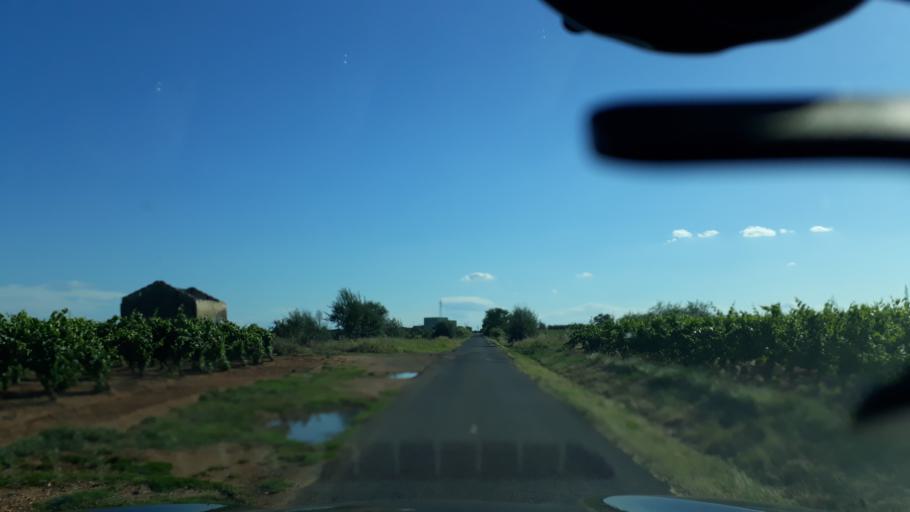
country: FR
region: Languedoc-Roussillon
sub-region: Departement de l'Herault
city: Agde
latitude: 43.3265
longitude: 3.4967
